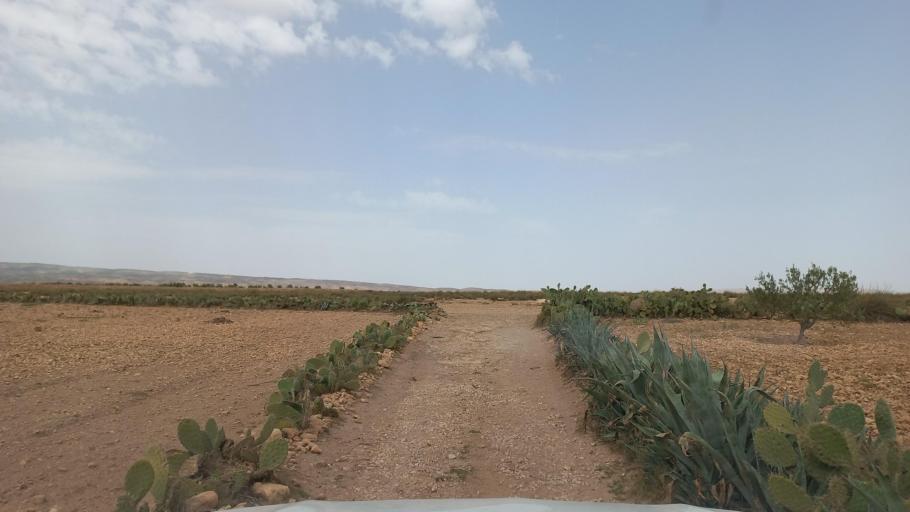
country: TN
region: Al Qasrayn
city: Kasserine
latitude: 35.2917
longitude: 9.0051
